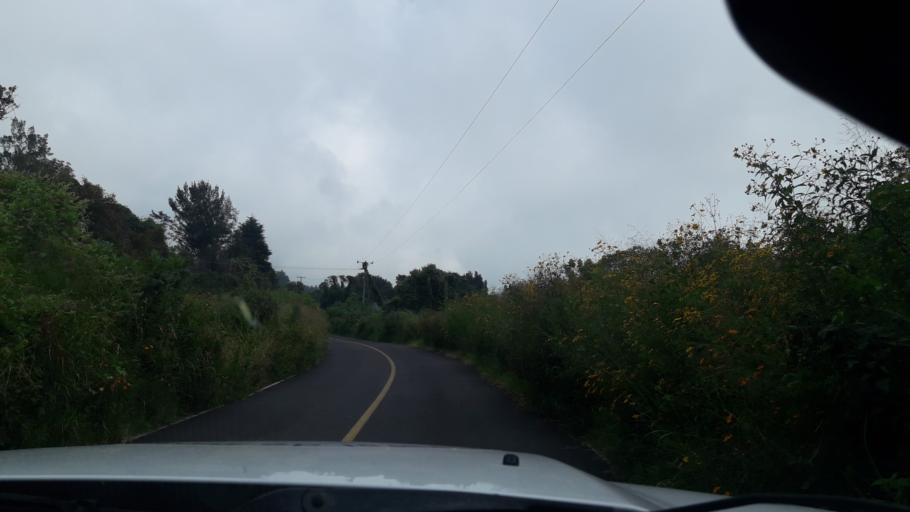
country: MX
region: Colima
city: Suchitlan
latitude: 19.4130
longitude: -103.6481
